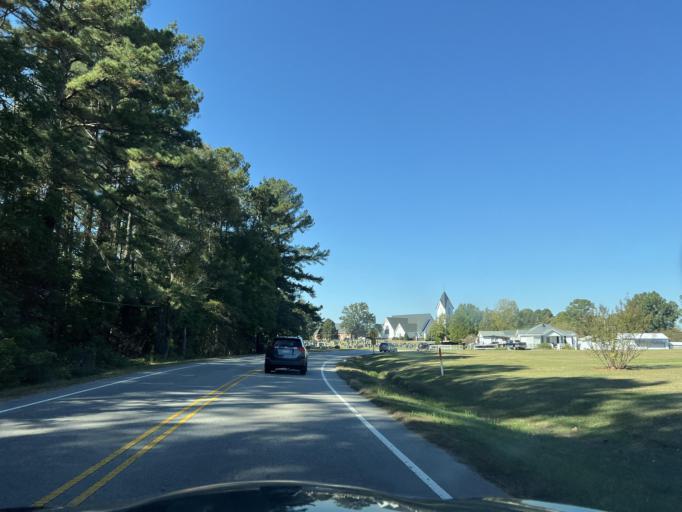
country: US
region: North Carolina
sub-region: Johnston County
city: Clayton
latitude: 35.6834
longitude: -78.5253
